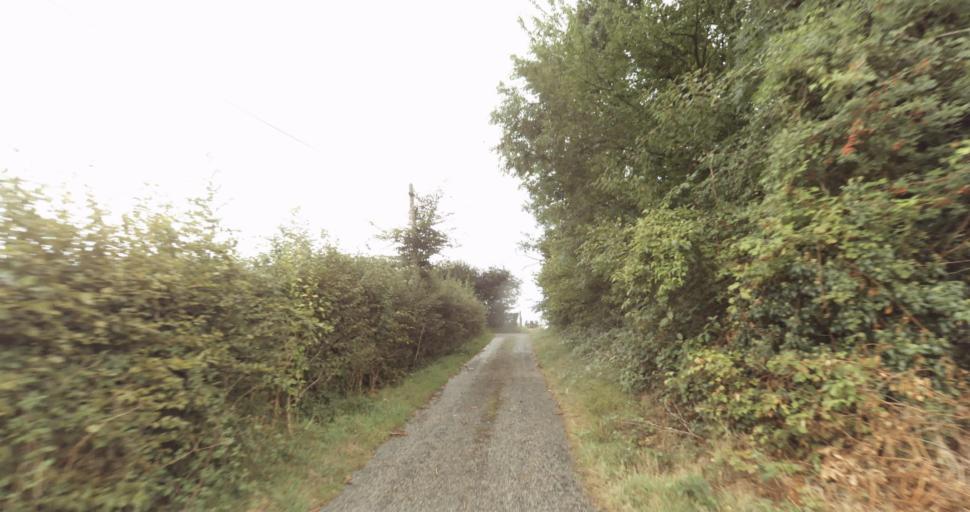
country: FR
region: Lower Normandy
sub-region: Departement de l'Orne
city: Vimoutiers
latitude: 48.8773
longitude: 0.1988
